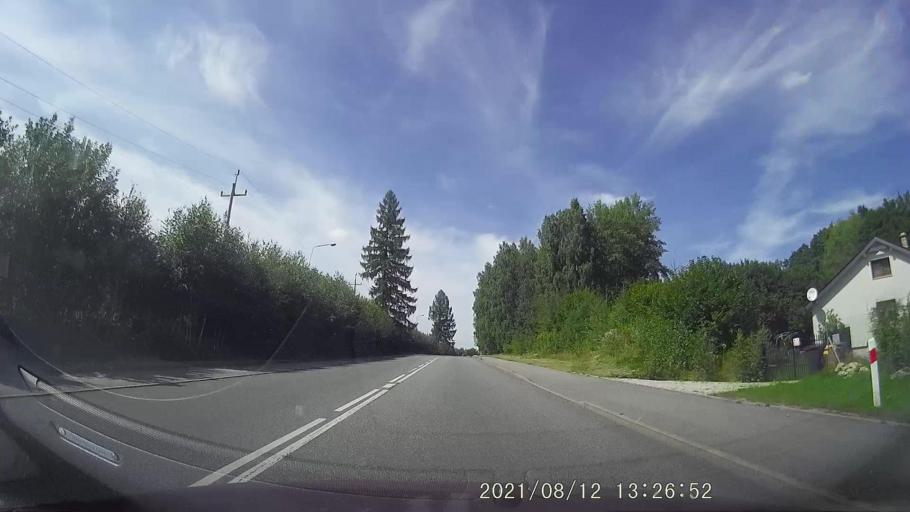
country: PL
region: Lower Silesian Voivodeship
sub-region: Powiat klodzki
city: Ladek-Zdroj
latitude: 50.3289
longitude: 16.8725
